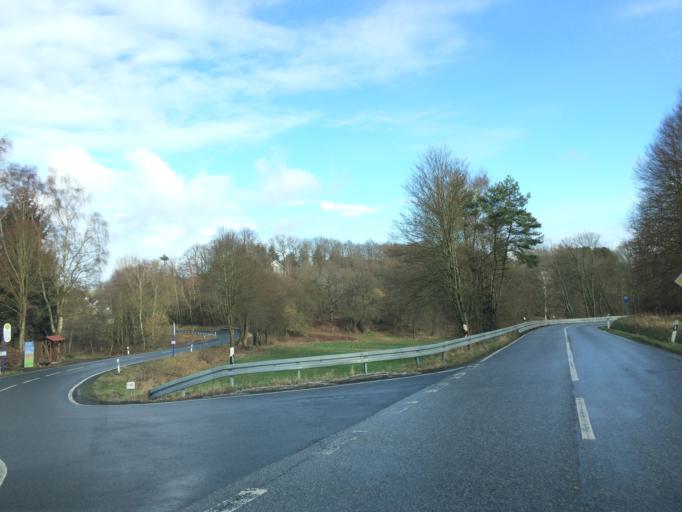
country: DE
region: Hesse
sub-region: Regierungsbezirk Darmstadt
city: Waldems
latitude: 50.3317
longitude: 8.3480
